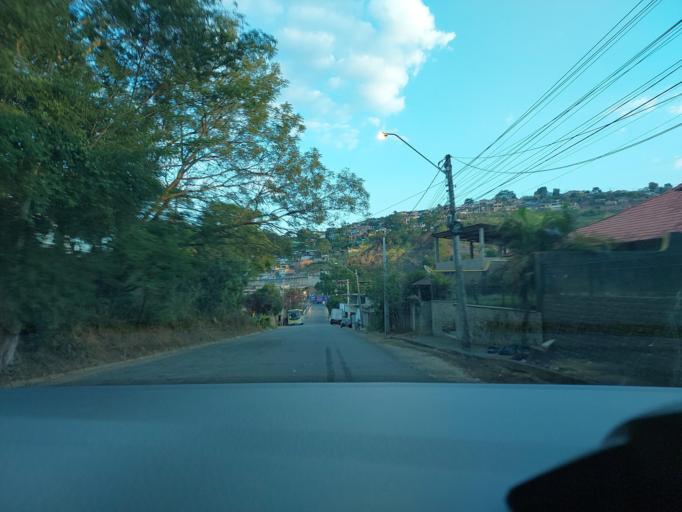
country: BR
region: Rio de Janeiro
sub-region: Natividade
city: Natividade
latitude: -21.2021
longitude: -42.1243
